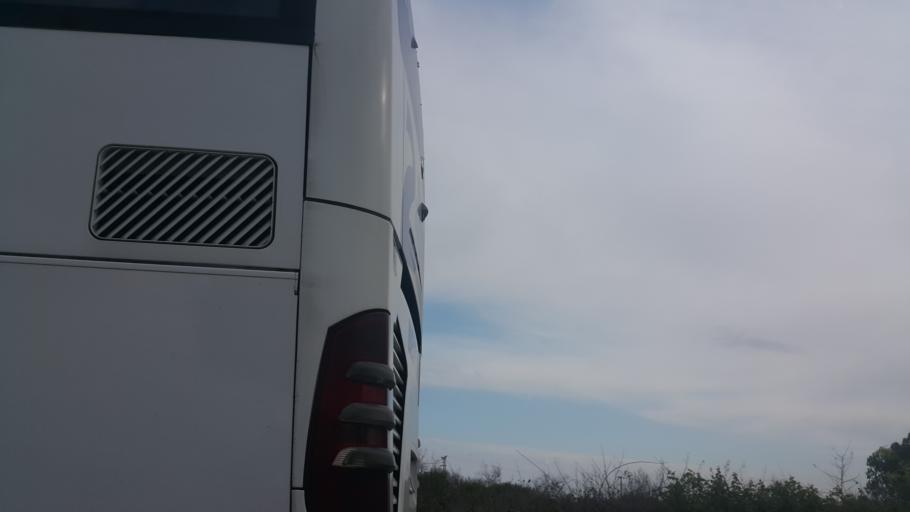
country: TR
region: Mersin
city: Yenice
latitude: 36.9764
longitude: 35.0700
